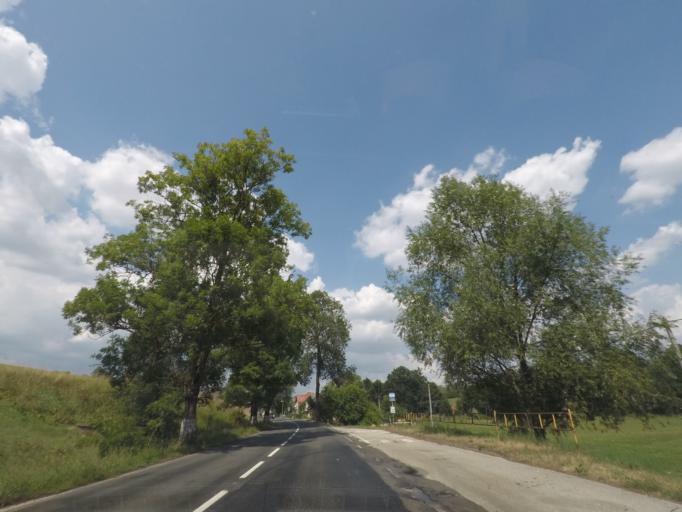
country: CZ
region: Kralovehradecky
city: Zadni Mostek
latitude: 50.5337
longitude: 15.6767
